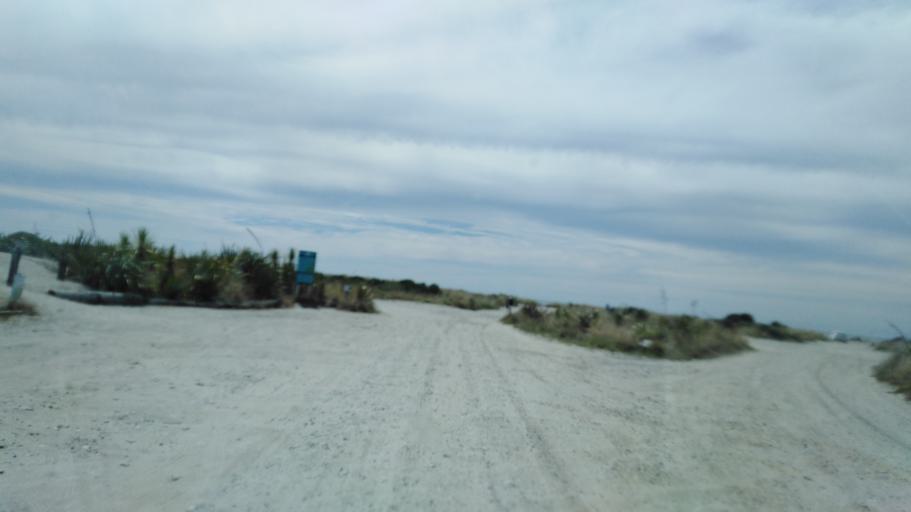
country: NZ
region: West Coast
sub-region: Buller District
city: Westport
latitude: -41.7346
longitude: 171.6056
